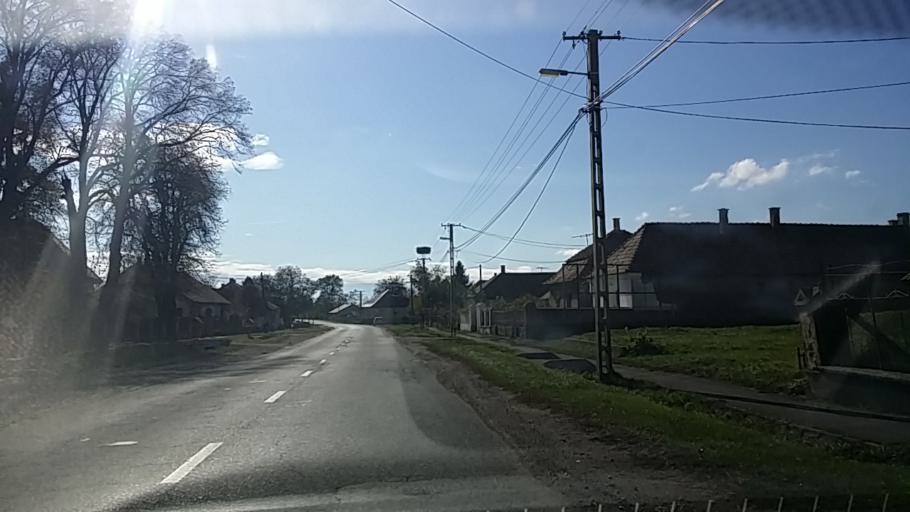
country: HU
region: Borsod-Abauj-Zemplen
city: Gonc
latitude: 48.4165
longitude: 21.2314
